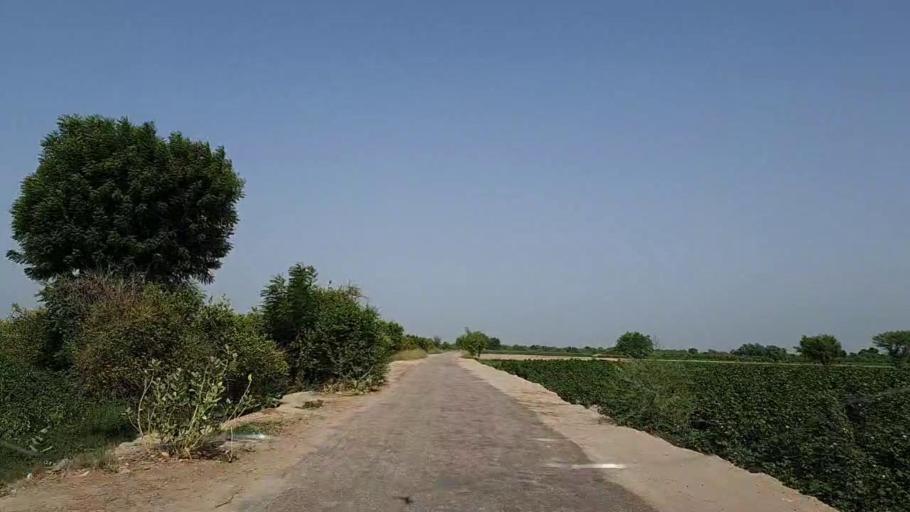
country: PK
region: Sindh
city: Kandiaro
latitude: 27.0726
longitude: 68.1456
